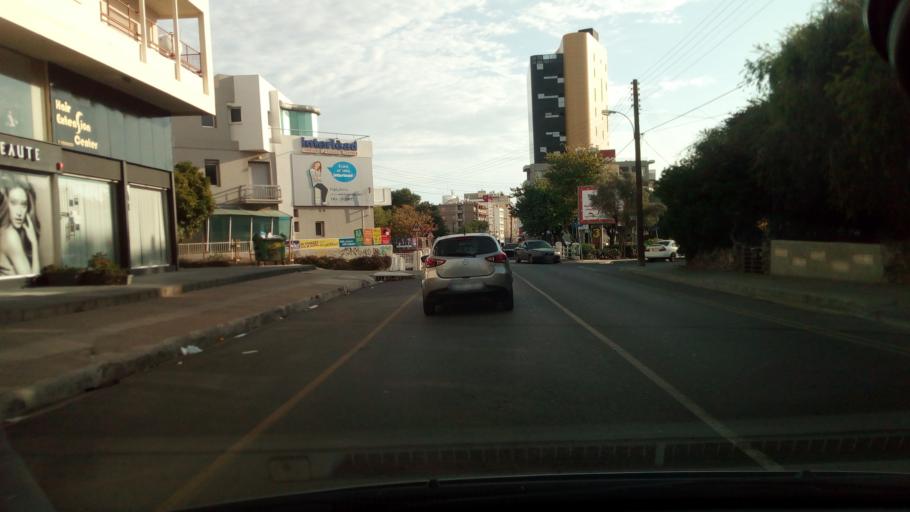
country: CY
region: Limassol
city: Limassol
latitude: 34.6885
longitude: 33.0369
